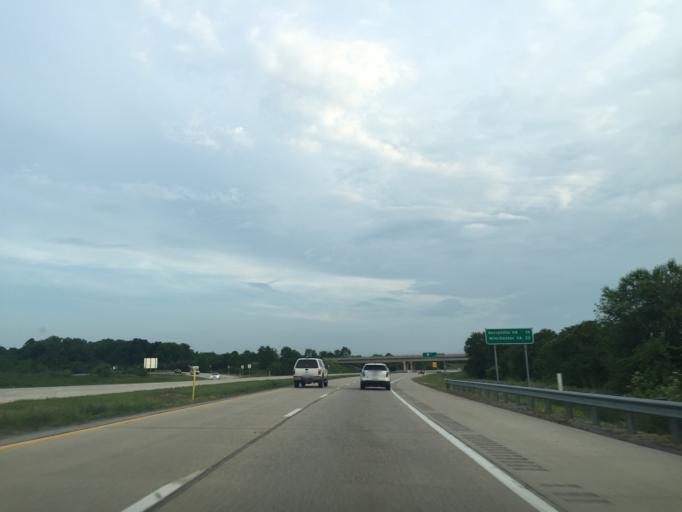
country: US
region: West Virginia
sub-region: Jefferson County
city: Charles Town
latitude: 39.2833
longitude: -77.8380
